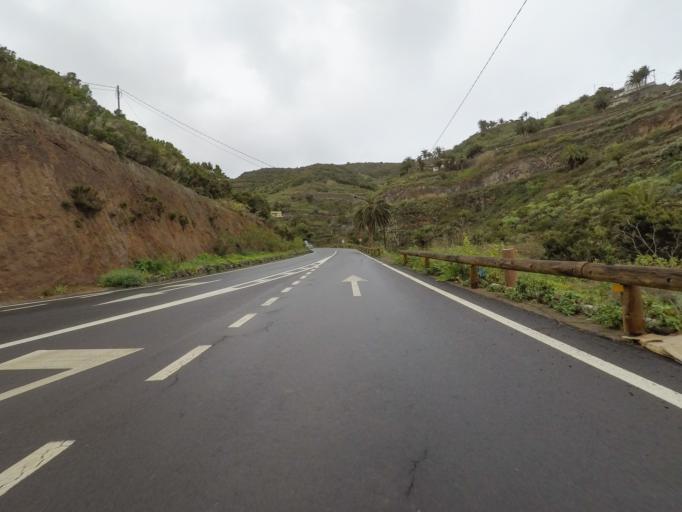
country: ES
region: Canary Islands
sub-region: Provincia de Santa Cruz de Tenerife
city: Agulo
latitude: 28.1839
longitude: -17.2239
